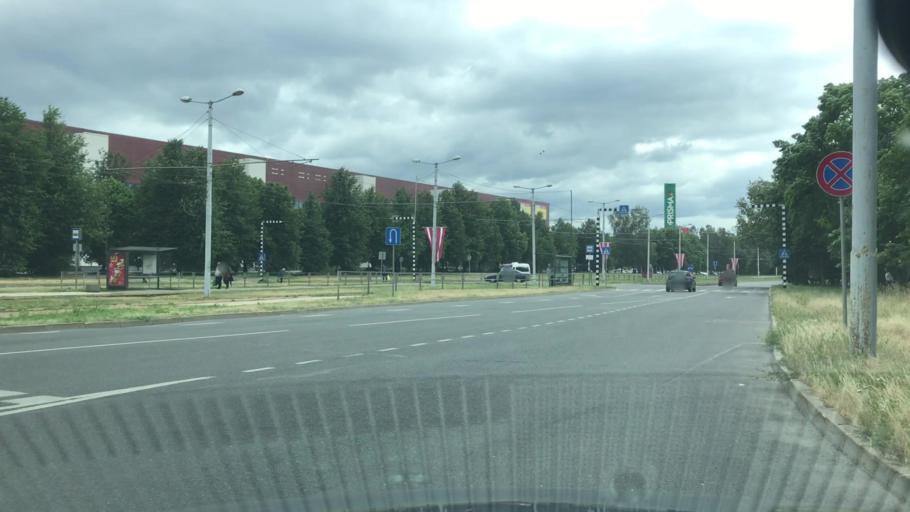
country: LV
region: Marupe
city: Marupe
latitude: 56.9573
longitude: 24.0343
